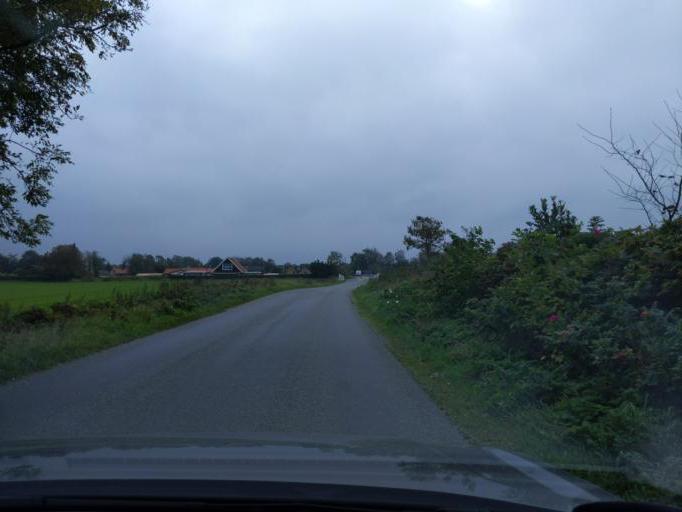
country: DK
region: Central Jutland
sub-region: Viborg Kommune
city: Viborg
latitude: 56.3657
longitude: 9.2963
